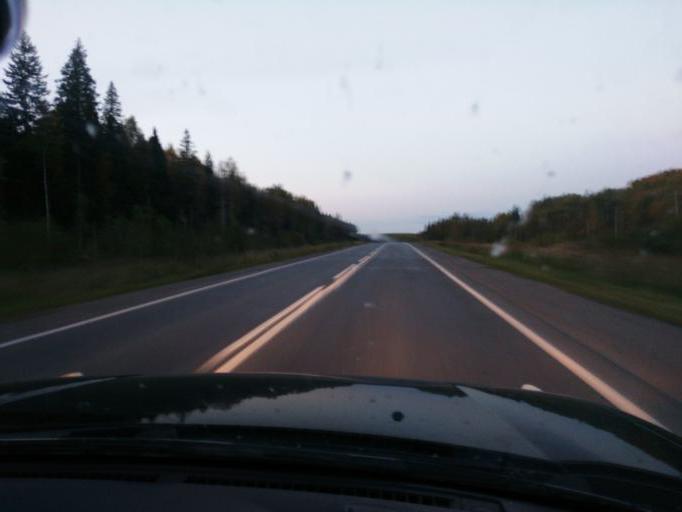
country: RU
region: Perm
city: Verkhnechusovskiye Gorodki
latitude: 58.2304
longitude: 57.2094
